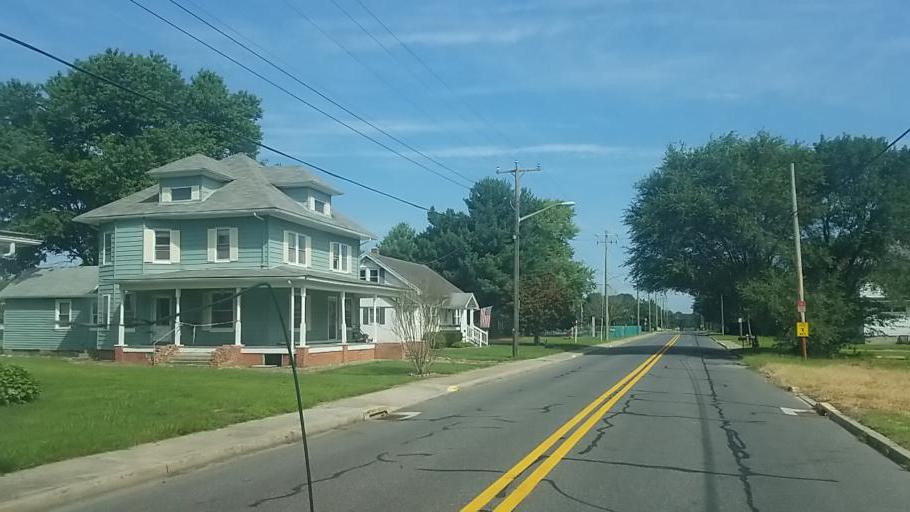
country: US
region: Delaware
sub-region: Sussex County
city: Selbyville
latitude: 38.5203
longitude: -75.2364
